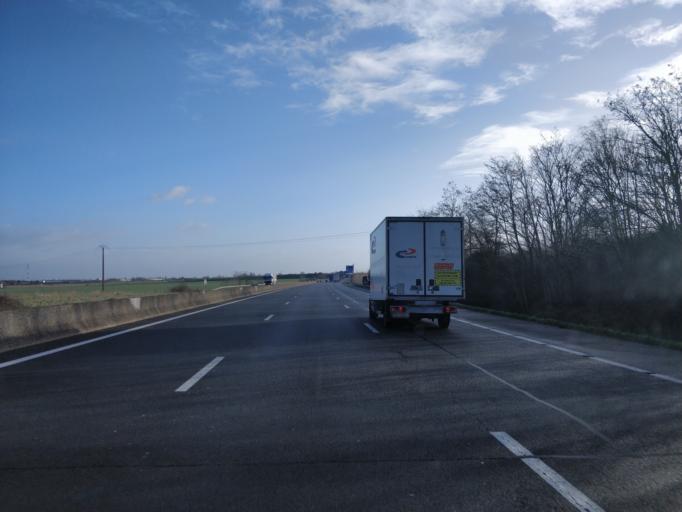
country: FR
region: Centre
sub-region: Departement du Loiret
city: La Chapelle-Saint-Mesmin
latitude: 47.9005
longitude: 1.8249
